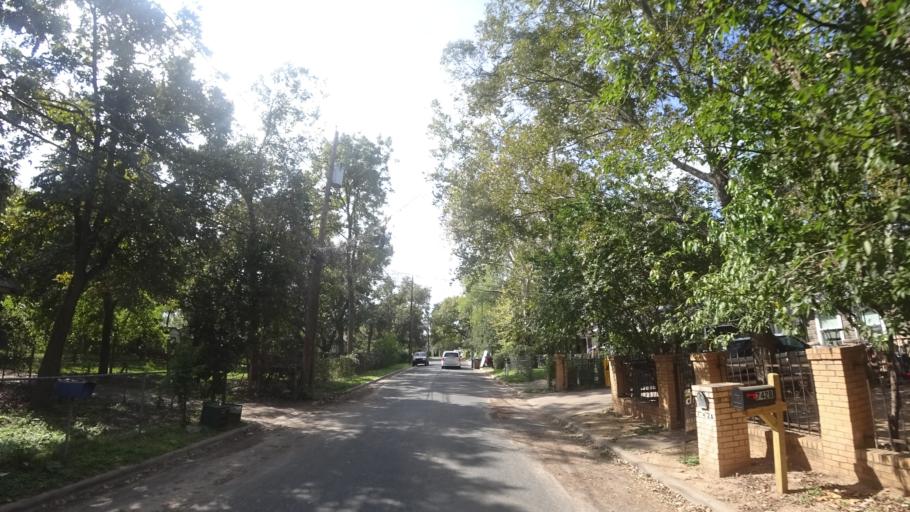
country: US
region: Texas
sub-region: Travis County
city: Austin
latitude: 30.2587
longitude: -97.7020
